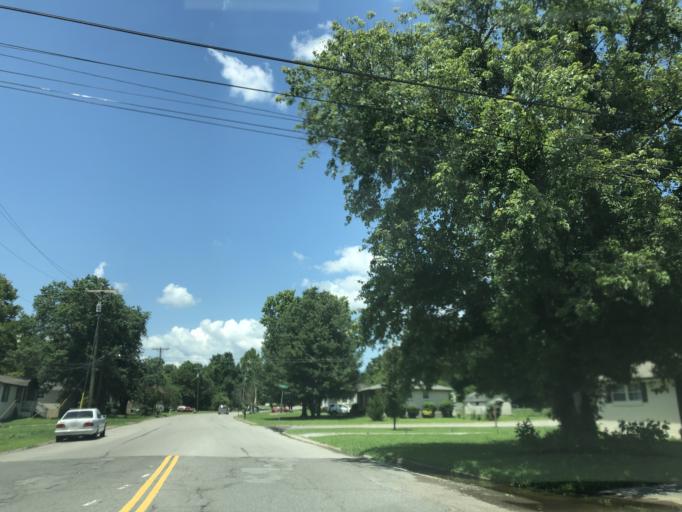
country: US
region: Tennessee
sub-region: Wilson County
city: Green Hill
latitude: 36.2162
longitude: -86.5880
